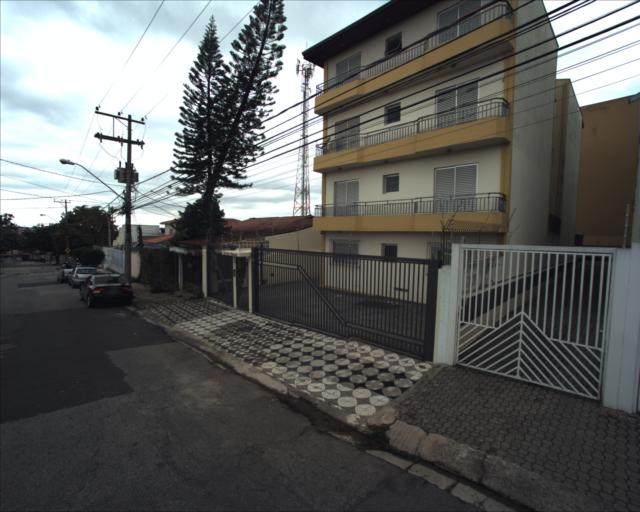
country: BR
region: Sao Paulo
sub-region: Sorocaba
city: Sorocaba
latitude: -23.5052
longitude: -47.4887
